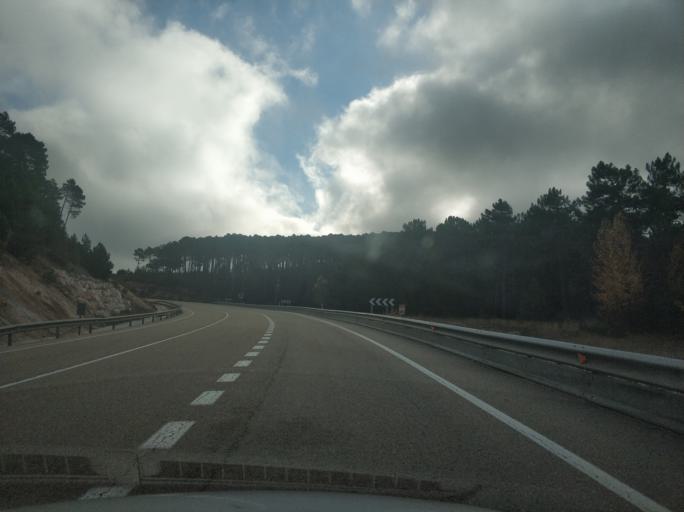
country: ES
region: Castille and Leon
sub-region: Provincia de Soria
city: Navaleno
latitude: 41.8283
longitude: -2.9665
